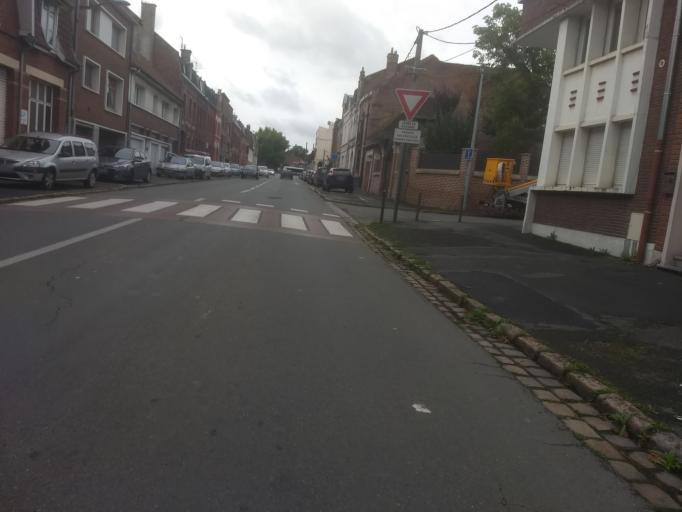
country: FR
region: Nord-Pas-de-Calais
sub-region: Departement du Pas-de-Calais
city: Saint-Nicolas
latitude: 50.2983
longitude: 2.7713
